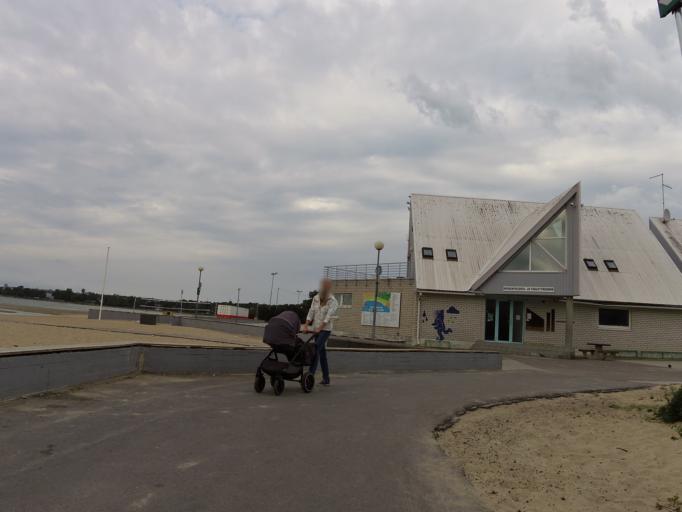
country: EE
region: Harju
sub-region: Tallinna linn
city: Tallinn
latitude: 59.4421
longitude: 24.6842
